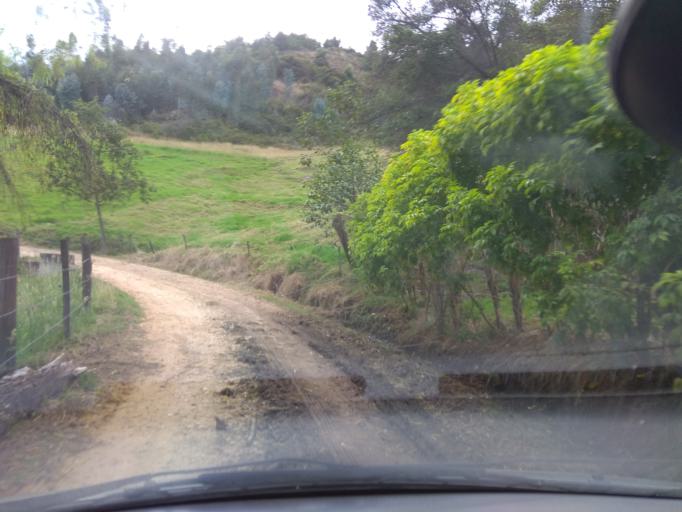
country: CO
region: Boyaca
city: Paipa
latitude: 5.8144
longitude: -73.0942
